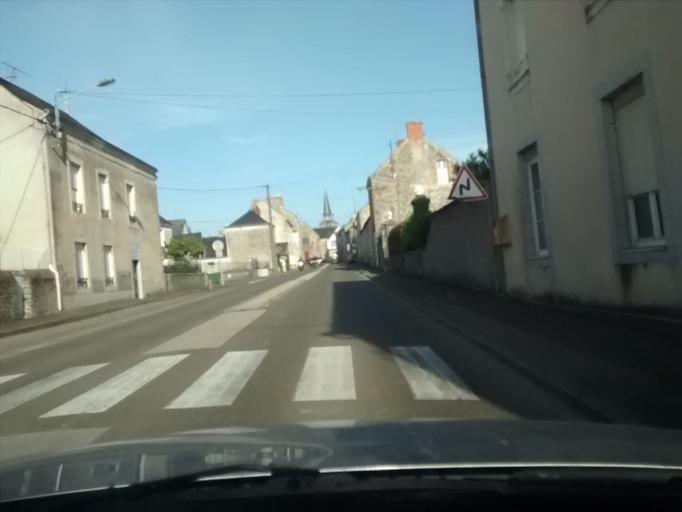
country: FR
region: Pays de la Loire
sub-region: Departement de la Mayenne
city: Vaiges
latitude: 48.0415
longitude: -0.4804
